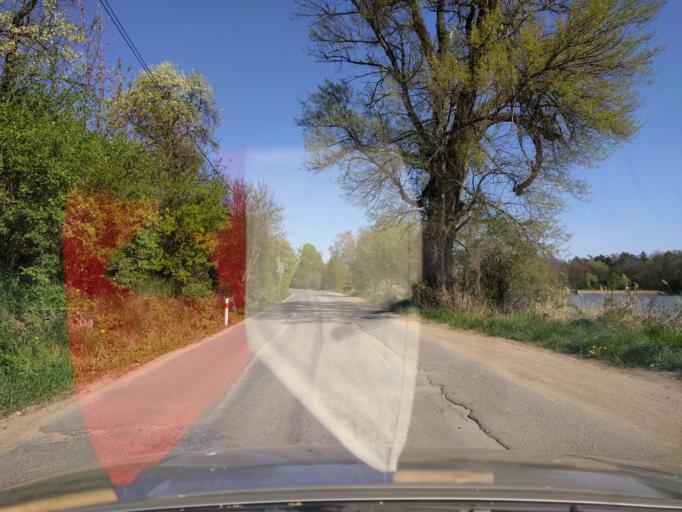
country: CZ
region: Central Bohemia
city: Cesky Brod
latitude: 50.0581
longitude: 14.8470
